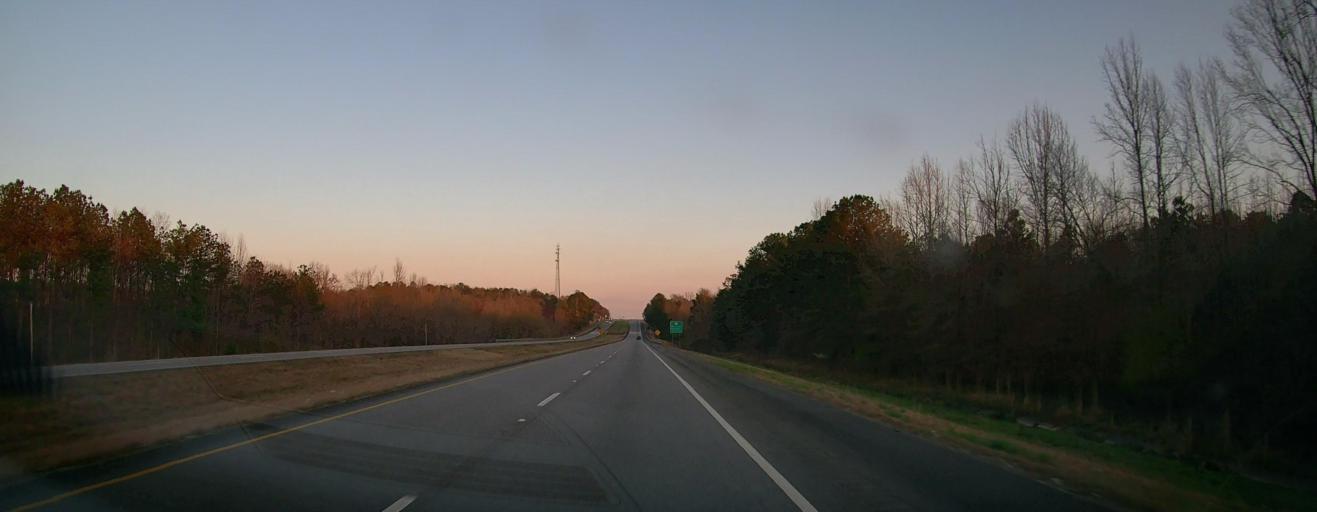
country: US
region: Alabama
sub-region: Coosa County
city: Goodwater
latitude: 33.0023
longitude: -86.0842
